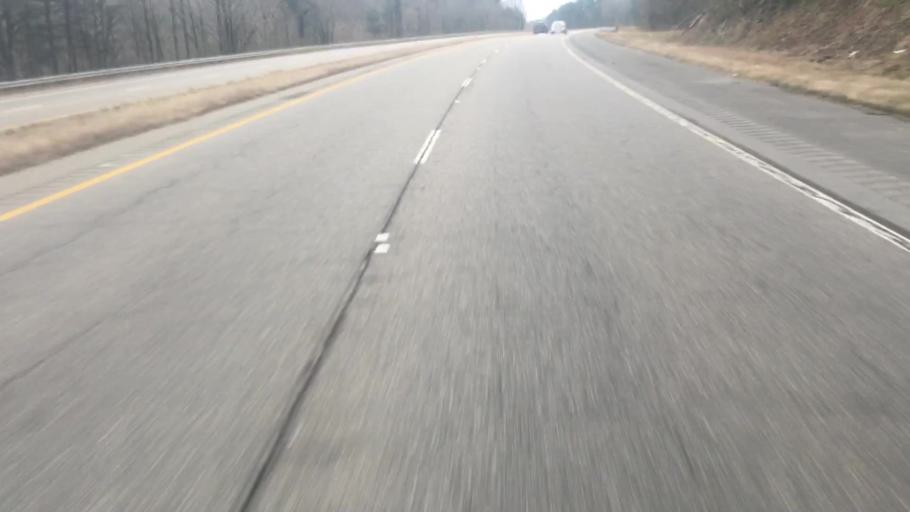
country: US
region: Alabama
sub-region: Walker County
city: Cordova
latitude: 33.8140
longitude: -87.1483
